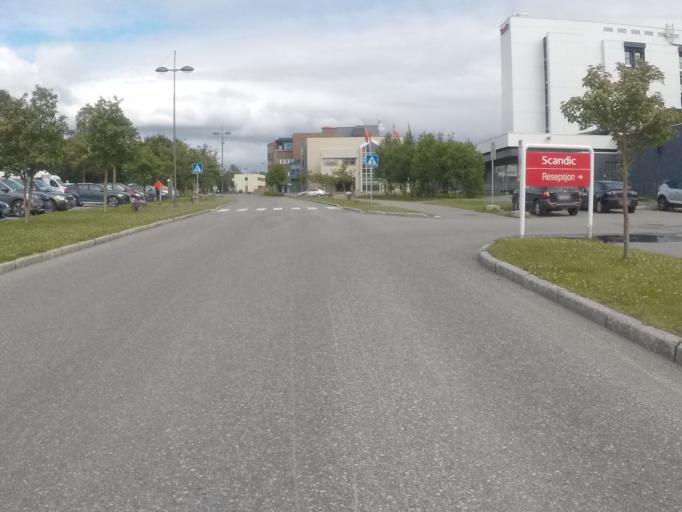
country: NO
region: Finnmark Fylke
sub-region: Alta
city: Alta
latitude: 69.9662
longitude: 23.2675
